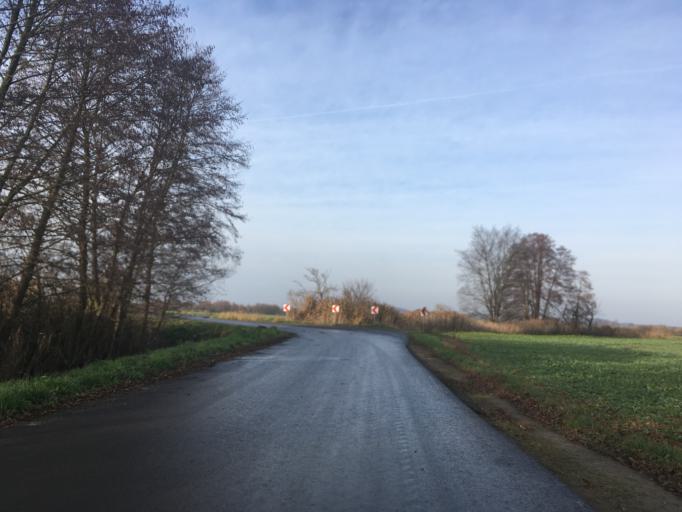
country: DE
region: Brandenburg
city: Bad Freienwalde
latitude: 52.7779
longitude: 14.0819
